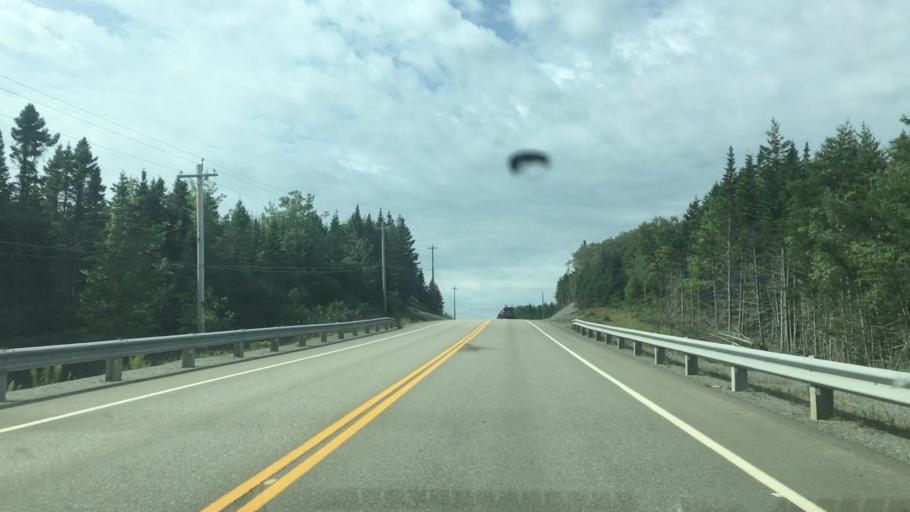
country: CA
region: Nova Scotia
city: Princeville
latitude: 45.6764
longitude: -60.7889
